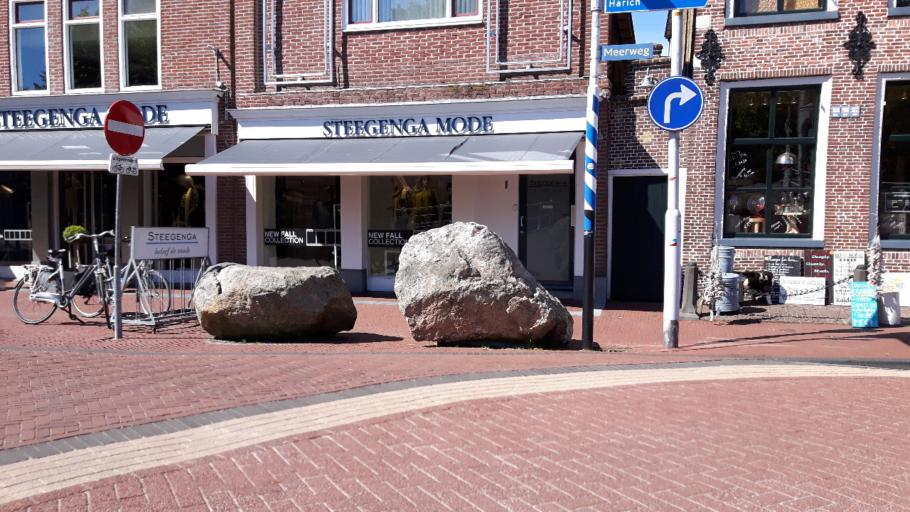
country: NL
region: Friesland
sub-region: Gemeente Gaasterlan-Sleat
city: Balk
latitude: 52.8991
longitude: 5.5829
